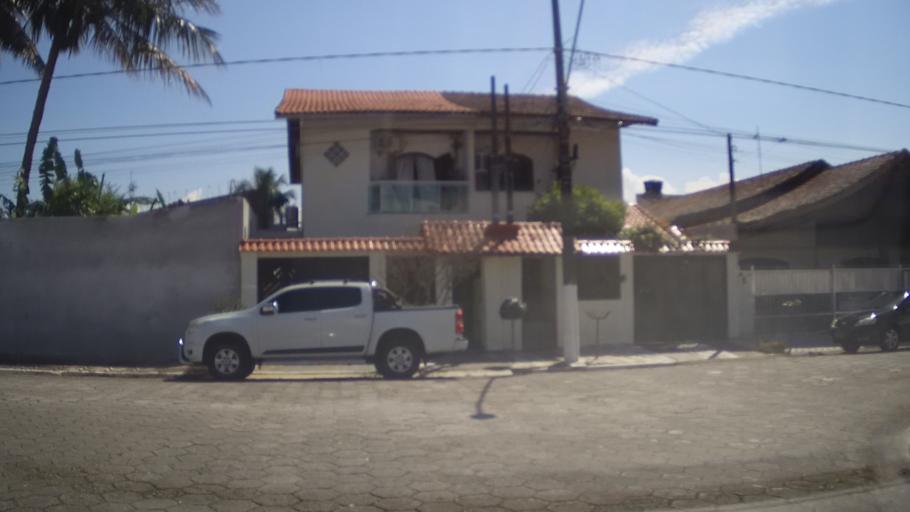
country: BR
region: Sao Paulo
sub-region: Praia Grande
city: Praia Grande
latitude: -24.0091
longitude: -46.3991
